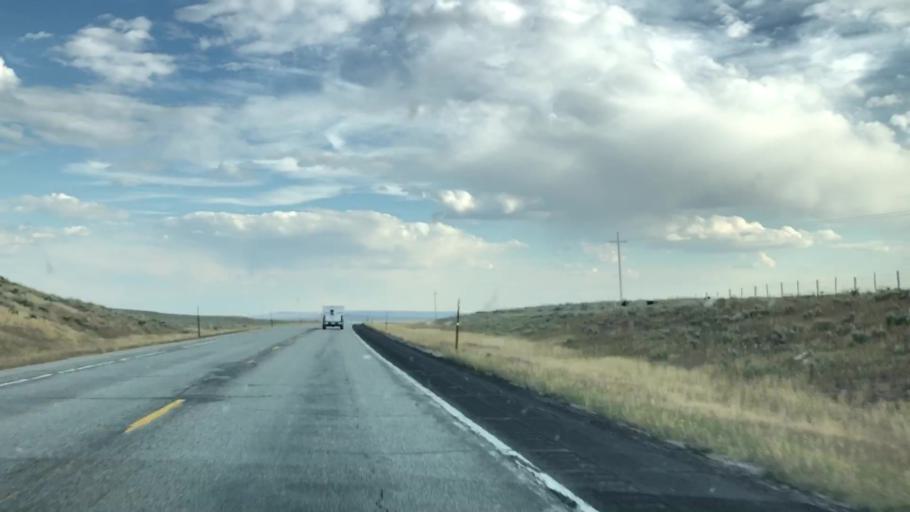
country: US
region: Wyoming
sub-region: Sublette County
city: Pinedale
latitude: 43.0568
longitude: -110.1564
